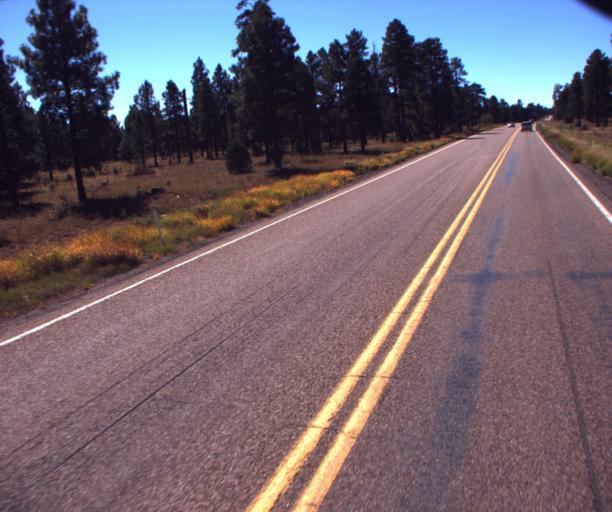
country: US
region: Arizona
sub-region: Navajo County
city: Heber-Overgaard
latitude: 34.4150
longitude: -110.6592
